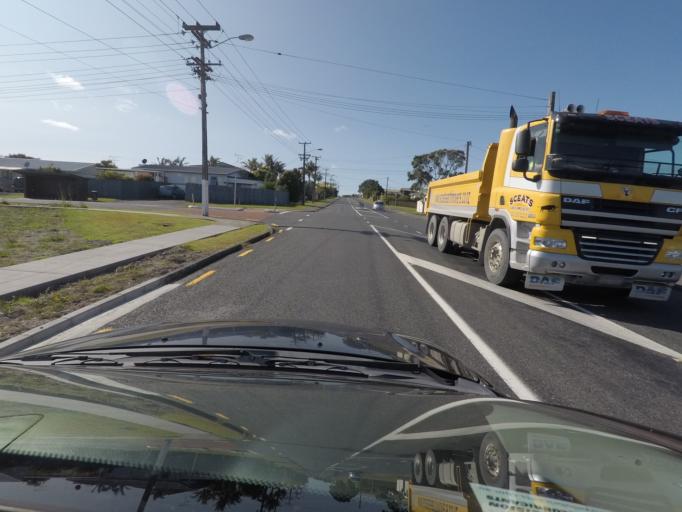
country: NZ
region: Auckland
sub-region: Auckland
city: Warkworth
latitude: -36.4243
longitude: 174.7276
